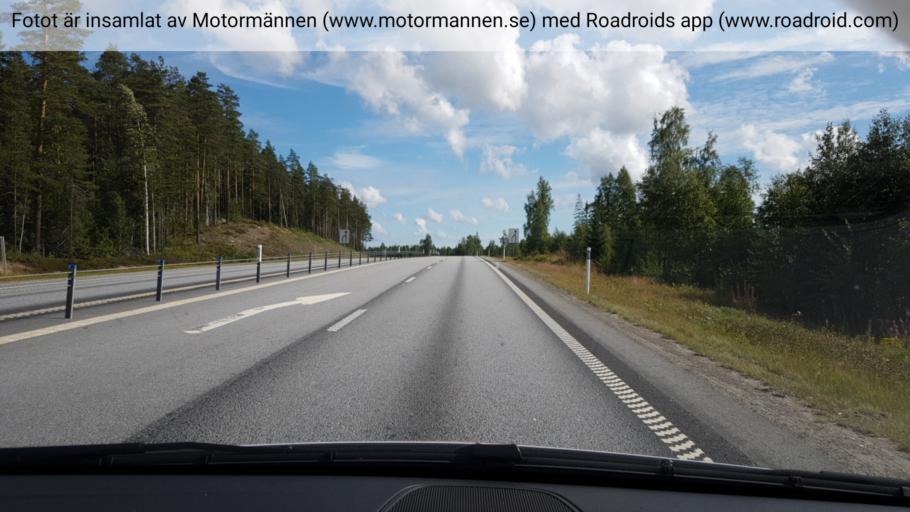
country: SE
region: Vaesterbotten
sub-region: Vannas Kommun
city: Vannasby
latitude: 63.8905
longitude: 19.9941
